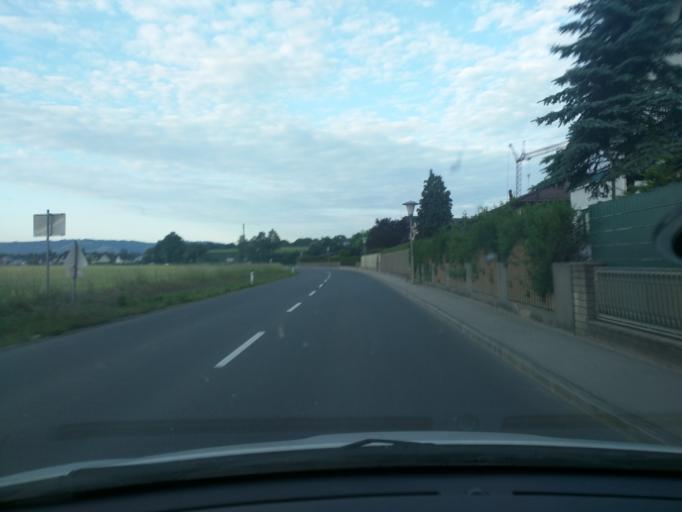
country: AT
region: Lower Austria
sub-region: Politischer Bezirk Amstetten
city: Zeillern
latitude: 48.0893
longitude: 14.8004
